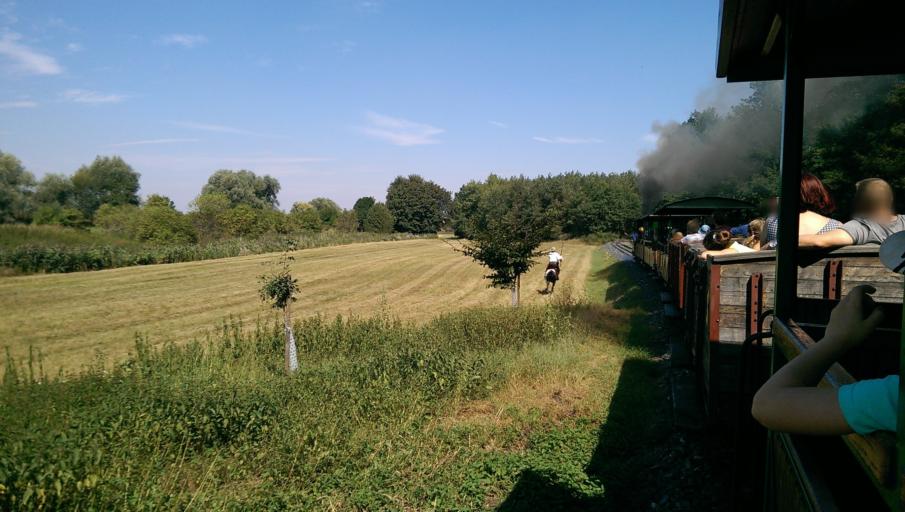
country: CZ
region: Central Bohemia
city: Stary Kolin
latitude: 50.0582
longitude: 15.2671
